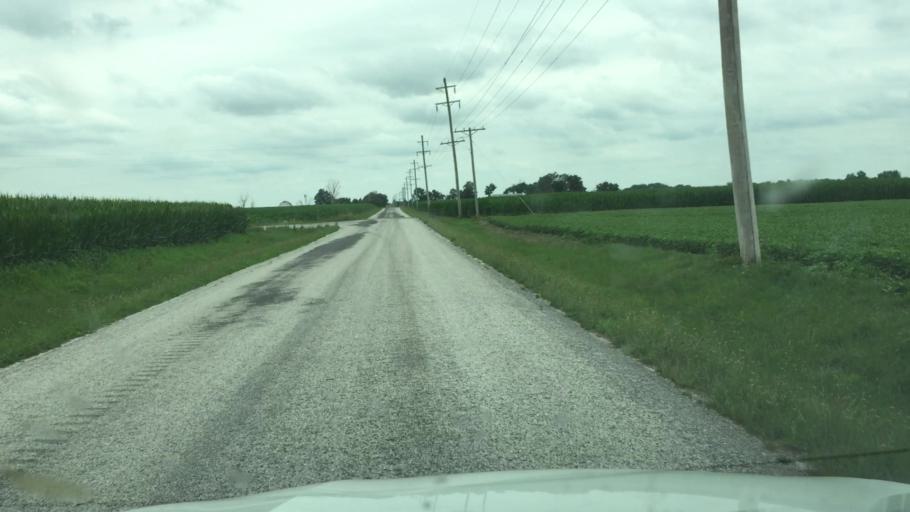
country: US
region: Illinois
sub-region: Hancock County
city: Carthage
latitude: 40.3942
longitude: -91.0826
